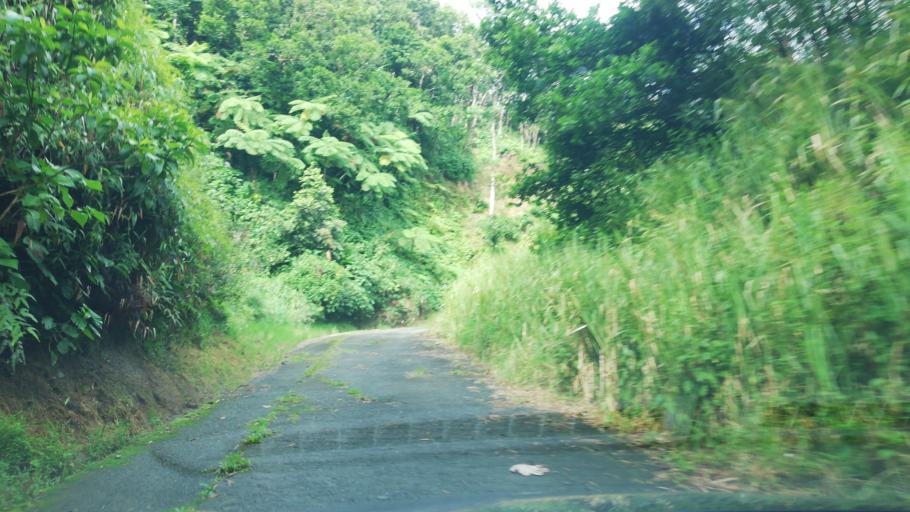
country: GP
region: Guadeloupe
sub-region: Guadeloupe
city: Bouillante
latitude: 16.1845
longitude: -61.7460
